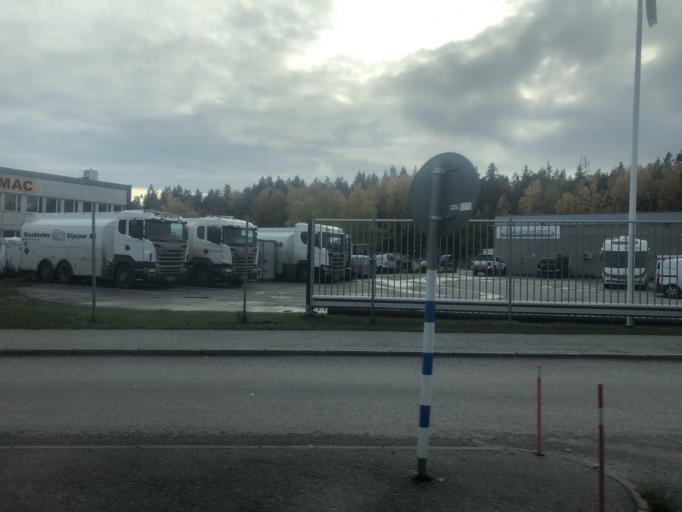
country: SE
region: Stockholm
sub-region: Jarfalla Kommun
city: Jakobsberg
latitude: 59.4063
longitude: 17.8426
